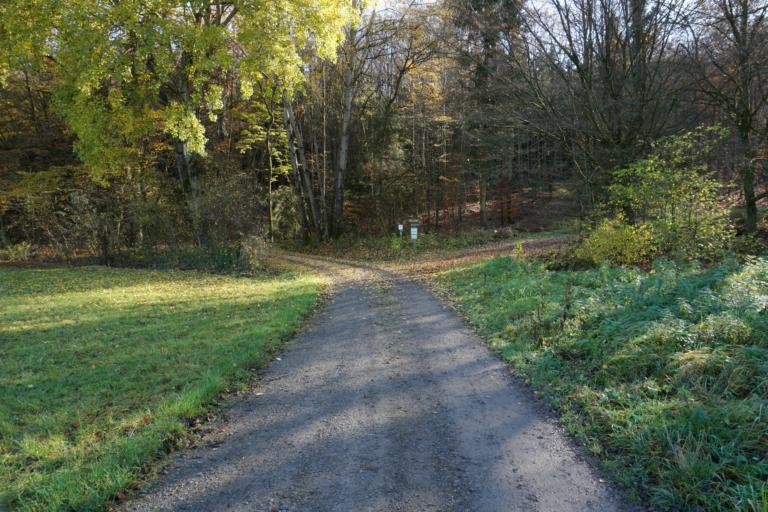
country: DE
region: Baden-Wuerttemberg
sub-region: Karlsruhe Region
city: Aglasterhausen
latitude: 49.3700
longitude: 9.0005
